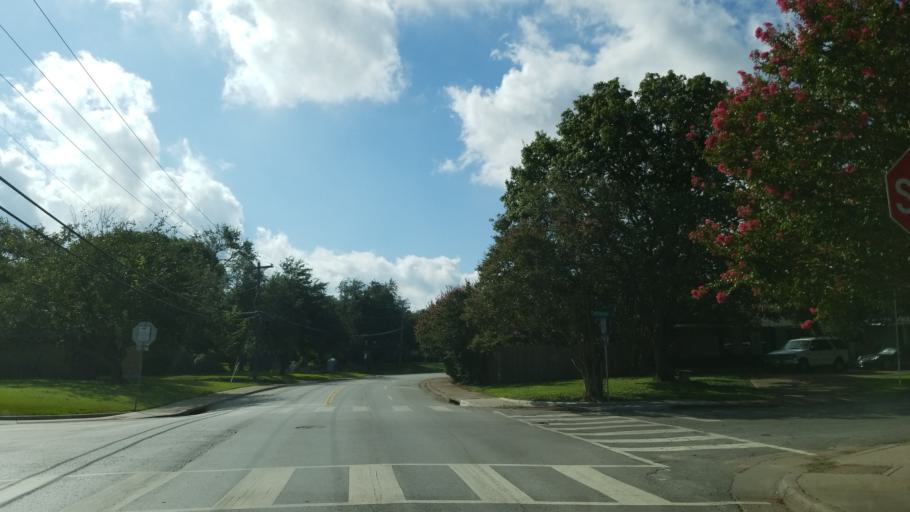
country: US
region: Texas
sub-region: Dallas County
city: Richardson
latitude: 32.9461
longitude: -96.7784
